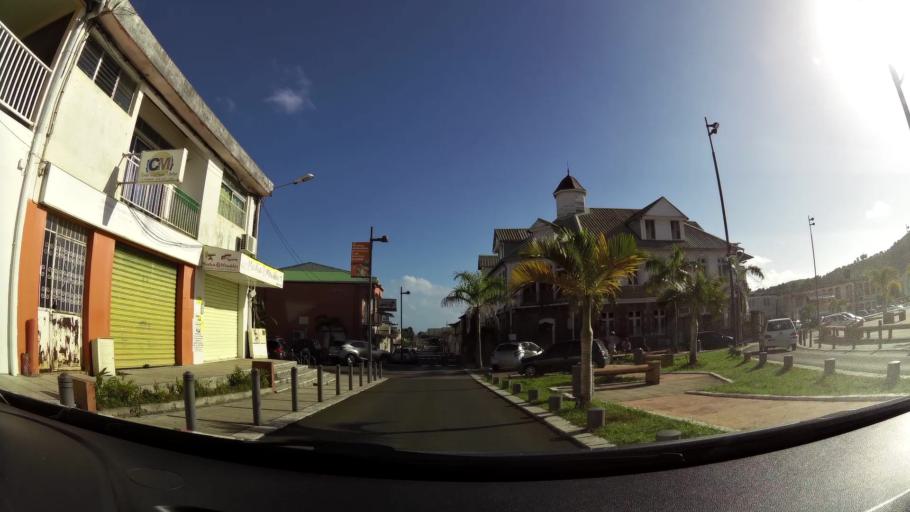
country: MQ
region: Martinique
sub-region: Martinique
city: Le Francois
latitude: 14.6152
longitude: -60.9032
